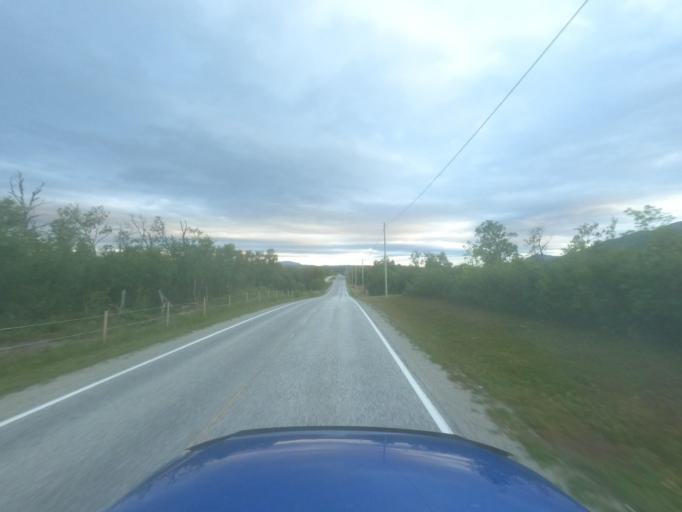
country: NO
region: Finnmark Fylke
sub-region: Porsanger
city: Lakselv
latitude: 70.0613
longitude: 24.9313
